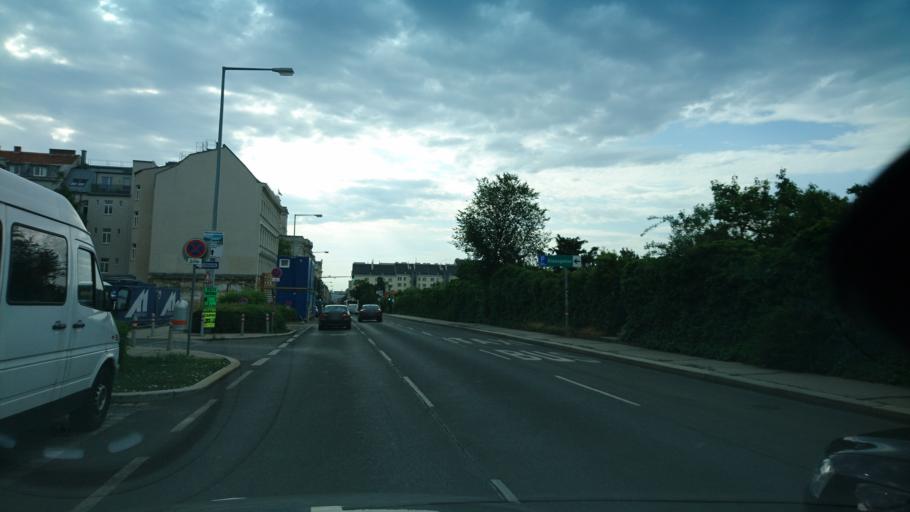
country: AT
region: Vienna
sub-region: Wien Stadt
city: Vienna
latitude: 48.2058
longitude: 16.3221
